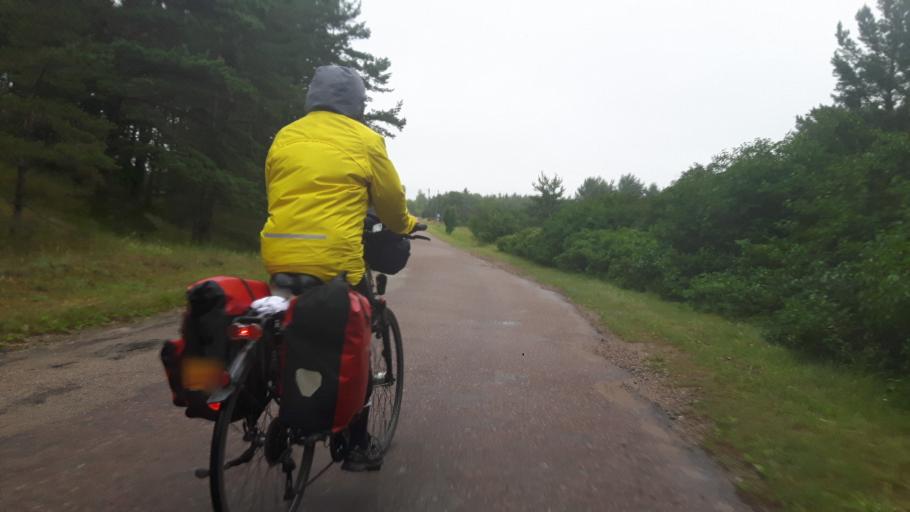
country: LV
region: Nica
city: Nica
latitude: 56.3834
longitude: 20.9915
